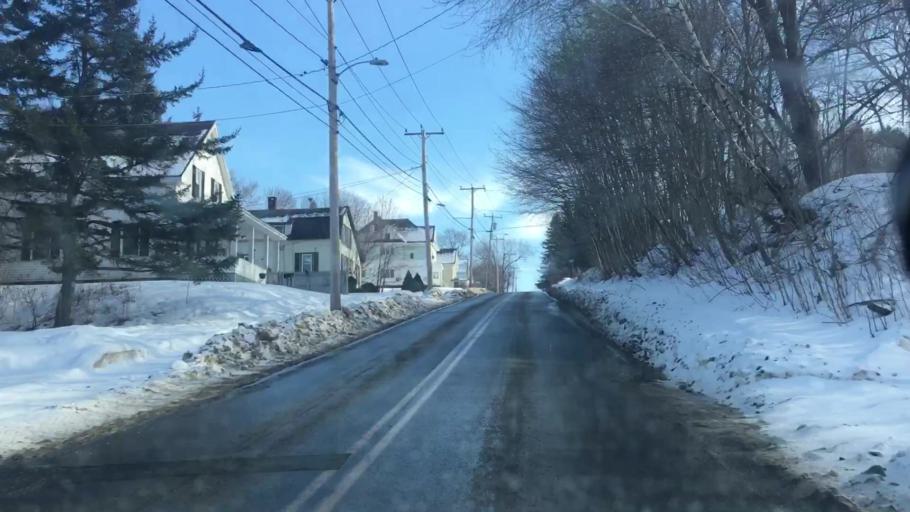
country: US
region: Maine
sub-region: Penobscot County
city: Bangor
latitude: 44.7696
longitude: -68.7781
